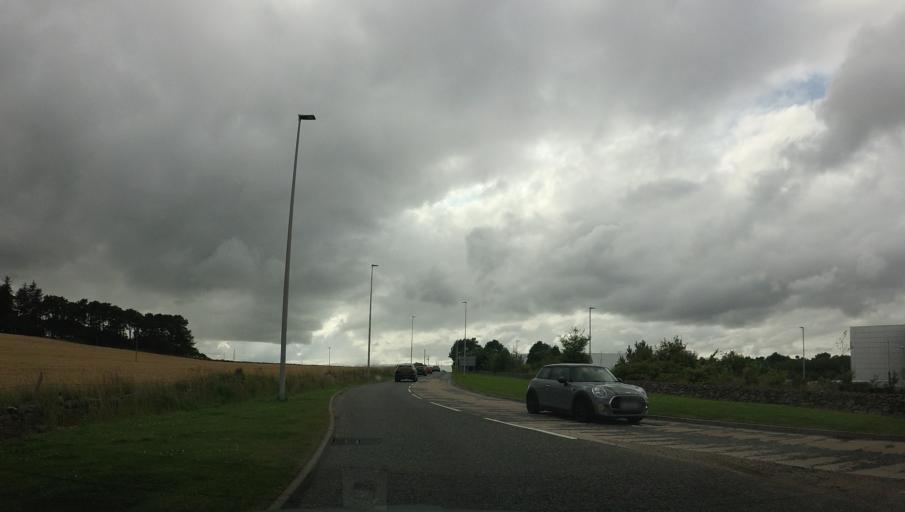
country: GB
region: Scotland
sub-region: Aberdeenshire
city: Westhill
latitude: 57.1442
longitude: -2.2914
